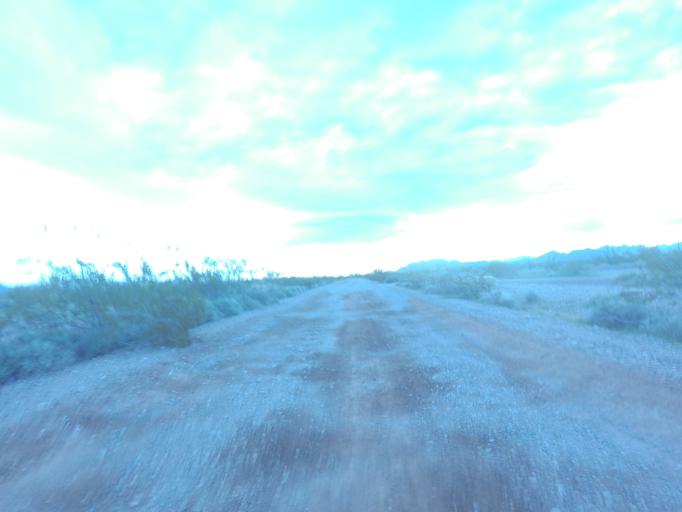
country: US
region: Arizona
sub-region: La Paz County
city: Quartzsite
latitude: 33.5357
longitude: -114.2089
